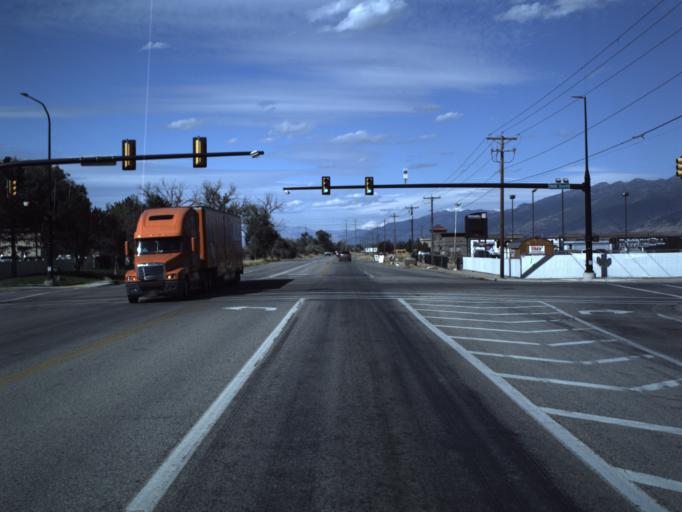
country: US
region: Utah
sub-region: Davis County
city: West Bountiful
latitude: 40.8742
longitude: -111.9300
